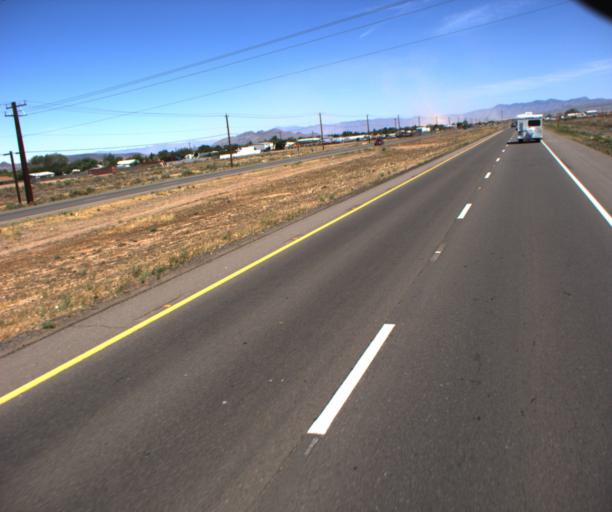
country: US
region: Arizona
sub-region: Mohave County
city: New Kingman-Butler
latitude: 35.2477
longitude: -113.9811
